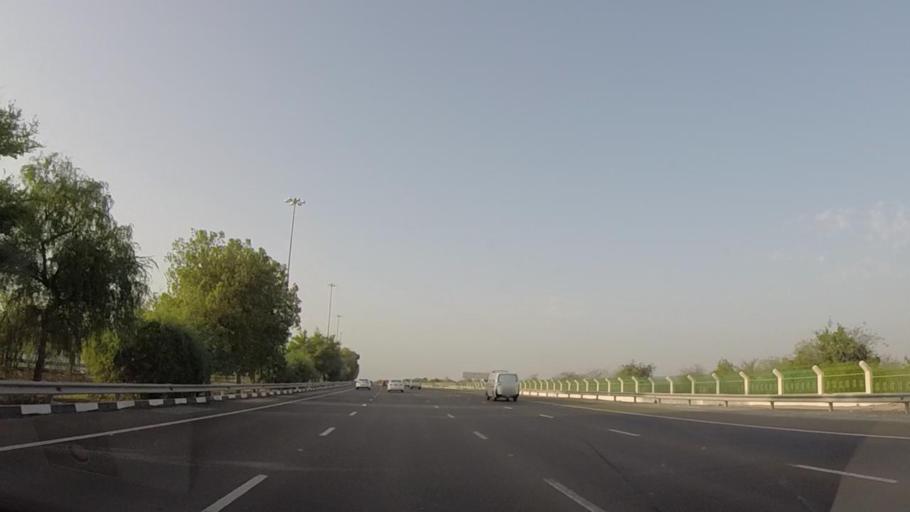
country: AE
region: Dubai
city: Dubai
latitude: 24.8522
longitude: 54.8981
